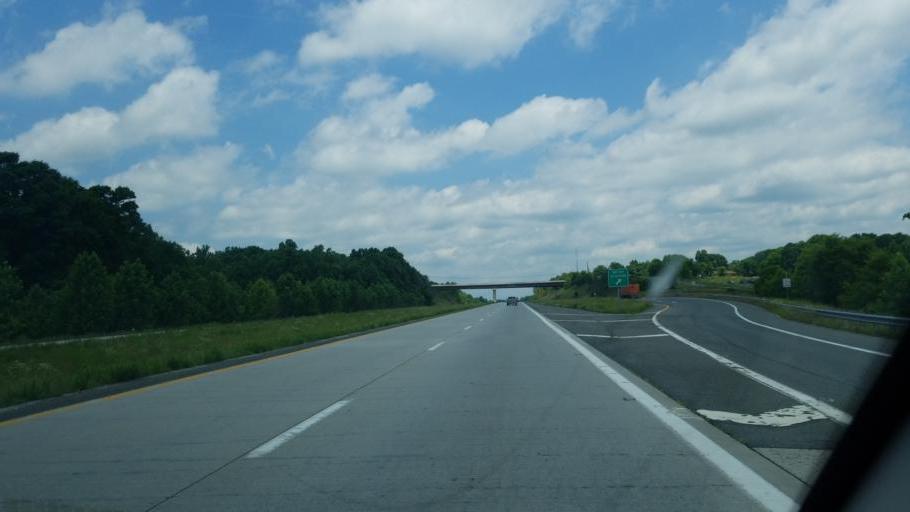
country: US
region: Virginia
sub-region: Amherst County
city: Madison Heights
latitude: 37.4392
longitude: -79.0763
